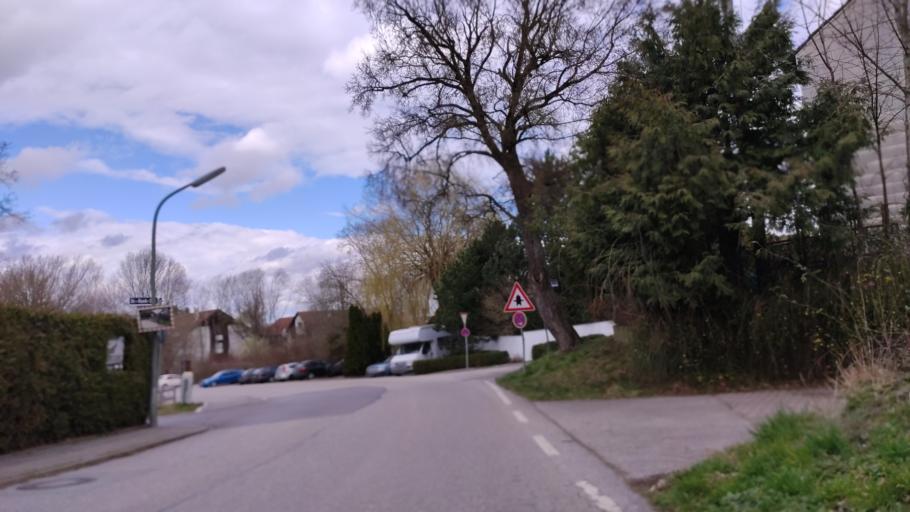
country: DE
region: Bavaria
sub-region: Upper Bavaria
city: Emmering
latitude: 48.1788
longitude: 11.3005
